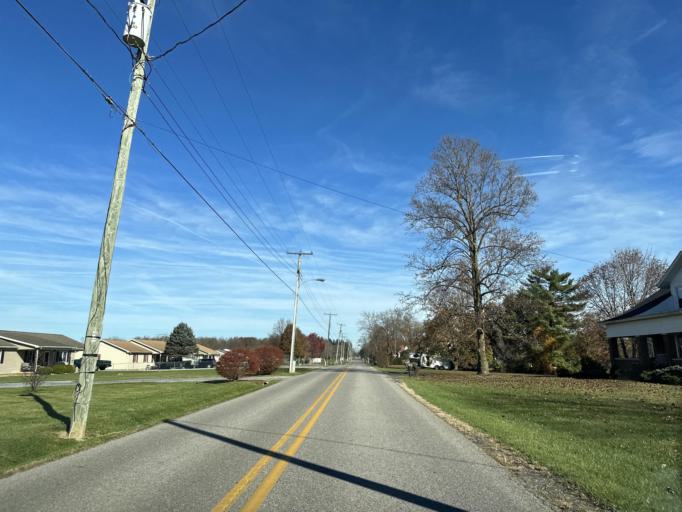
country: US
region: Virginia
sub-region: Augusta County
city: Crimora
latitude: 38.2047
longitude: -78.9039
